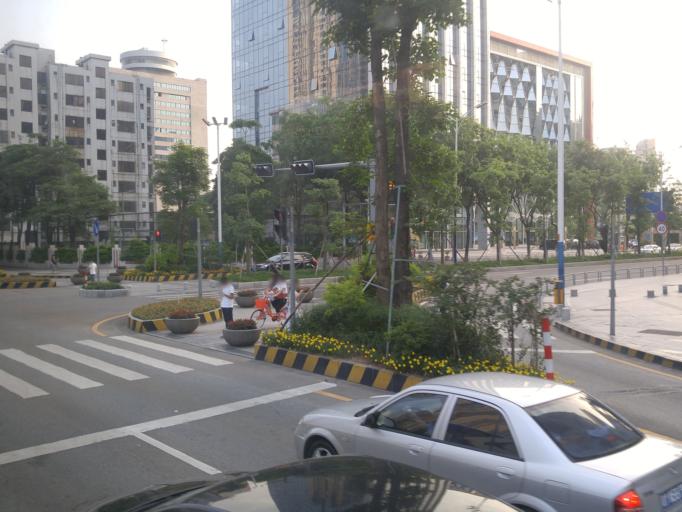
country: CN
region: Guangdong
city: Foshan
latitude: 23.0610
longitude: 113.1401
